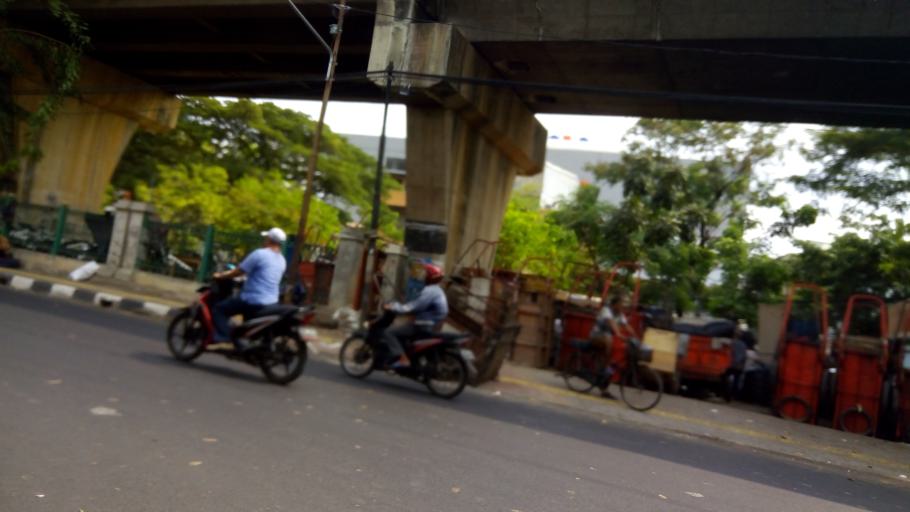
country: ID
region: Jakarta Raya
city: Jakarta
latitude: -6.1557
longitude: 106.8278
